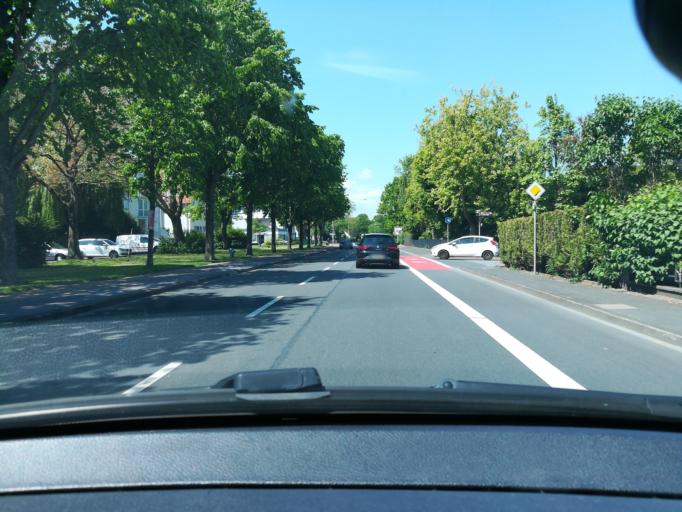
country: DE
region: North Rhine-Westphalia
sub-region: Regierungsbezirk Detmold
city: Oerlinghausen
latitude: 51.9942
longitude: 8.6026
